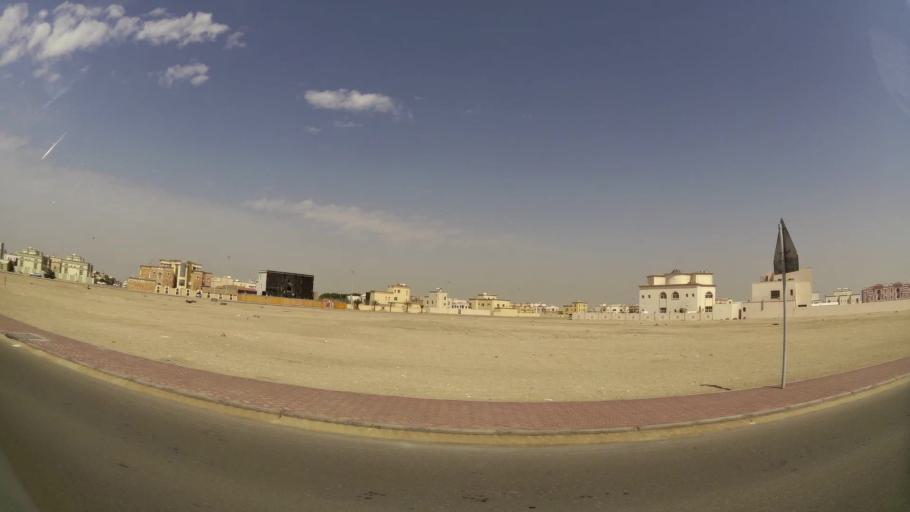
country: AE
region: Abu Dhabi
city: Abu Dhabi
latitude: 24.3139
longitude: 54.5414
